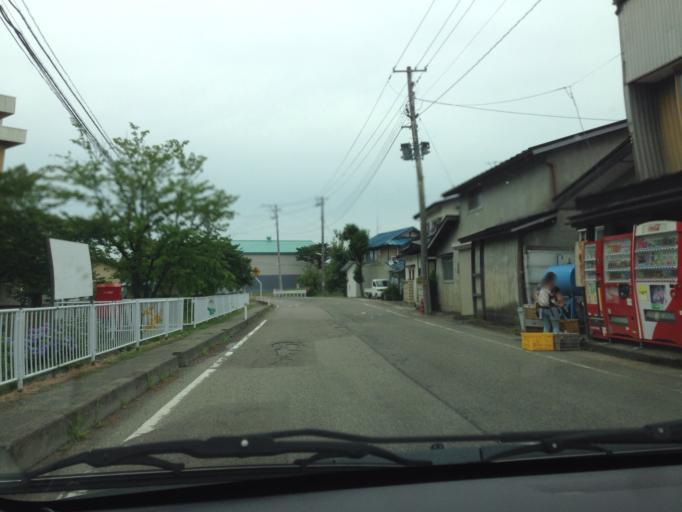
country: JP
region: Fukushima
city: Kitakata
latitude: 37.5630
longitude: 139.8719
